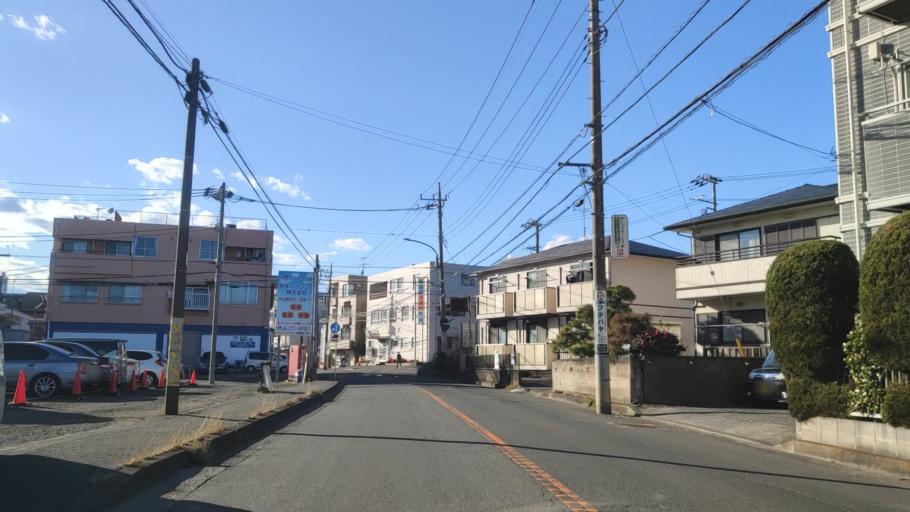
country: JP
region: Tokyo
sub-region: Machida-shi
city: Machida
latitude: 35.5186
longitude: 139.5468
